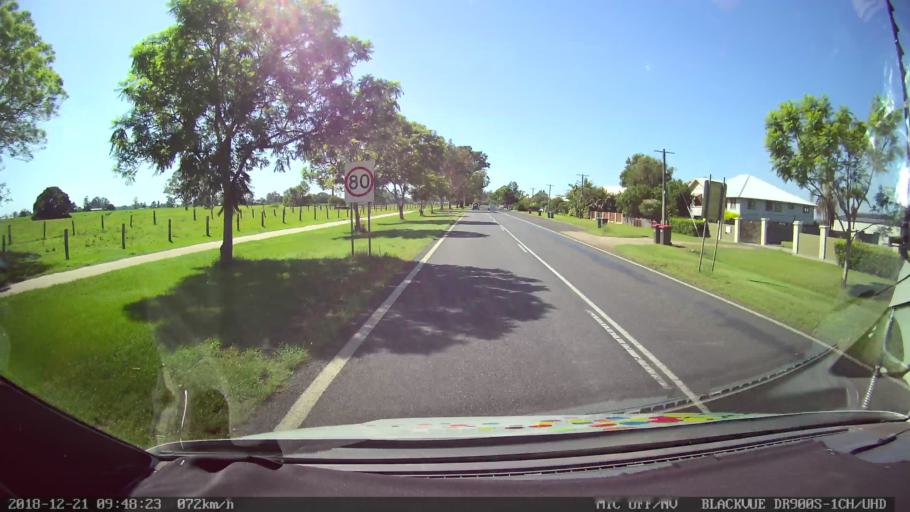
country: AU
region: New South Wales
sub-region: Clarence Valley
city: Grafton
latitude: -29.6525
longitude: 152.9332
